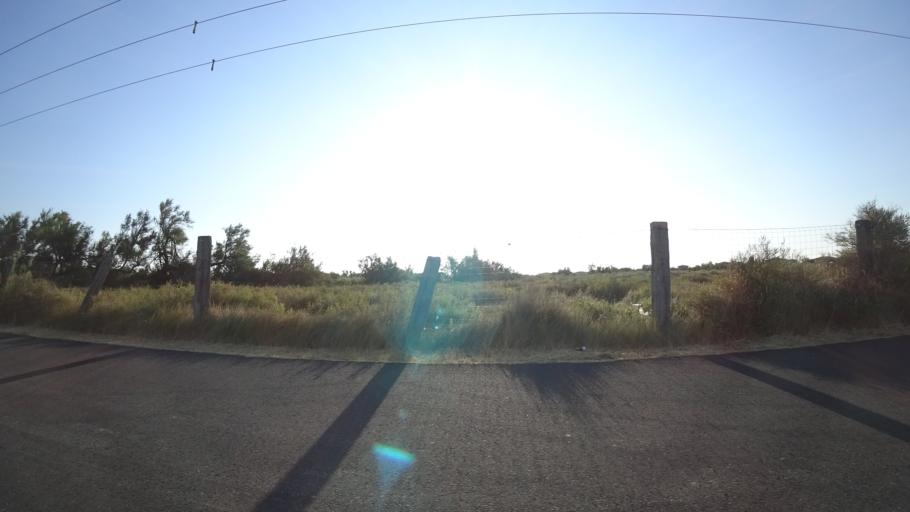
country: FR
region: Languedoc-Roussillon
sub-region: Departement des Pyrenees-Orientales
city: Torreilles
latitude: 42.7652
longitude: 3.0190
